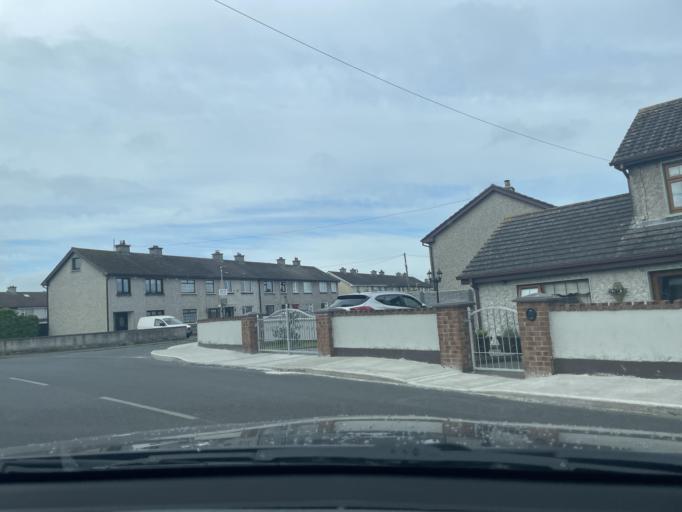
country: IE
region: Leinster
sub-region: County Carlow
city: Bagenalstown
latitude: 52.6989
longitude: -6.9636
